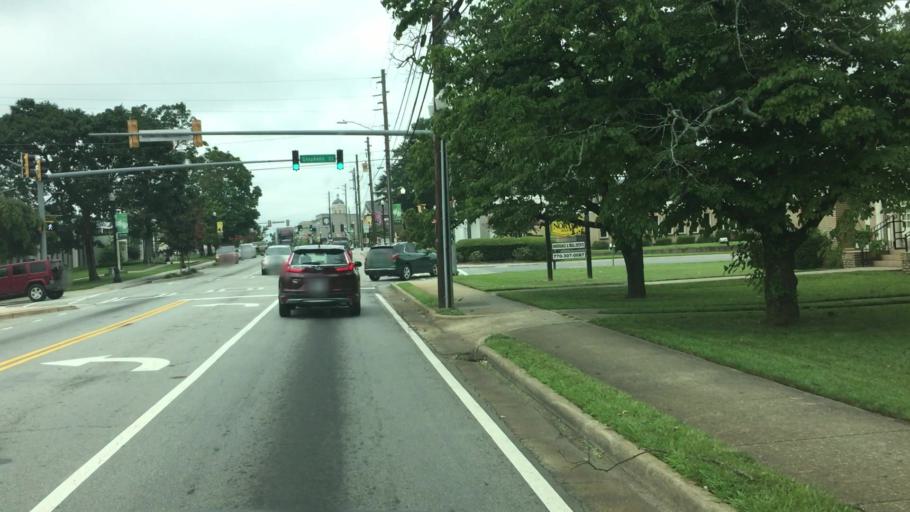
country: US
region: Georgia
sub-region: Barrow County
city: Winder
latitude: 33.9943
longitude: -83.7175
